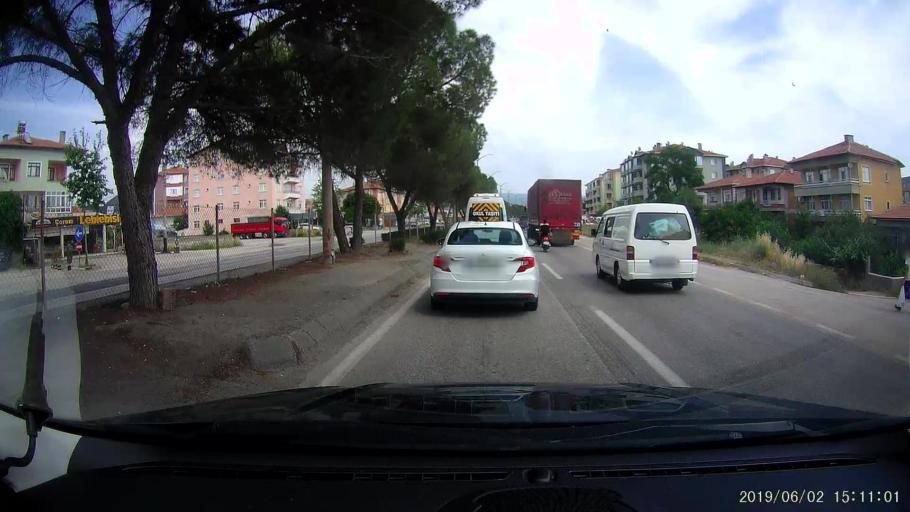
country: TR
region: Corum
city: Osmancik
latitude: 40.9785
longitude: 34.8065
